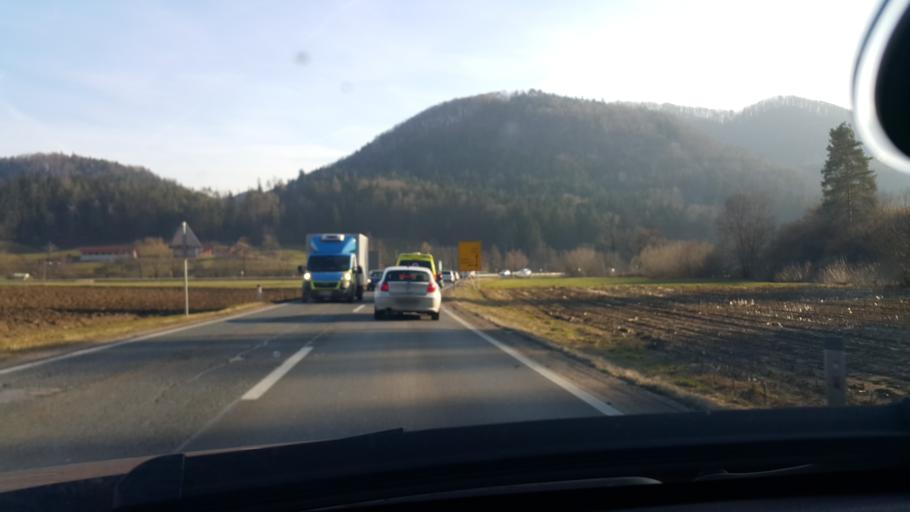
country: SI
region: Dobrna
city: Dobrna
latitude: 46.3256
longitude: 15.1833
